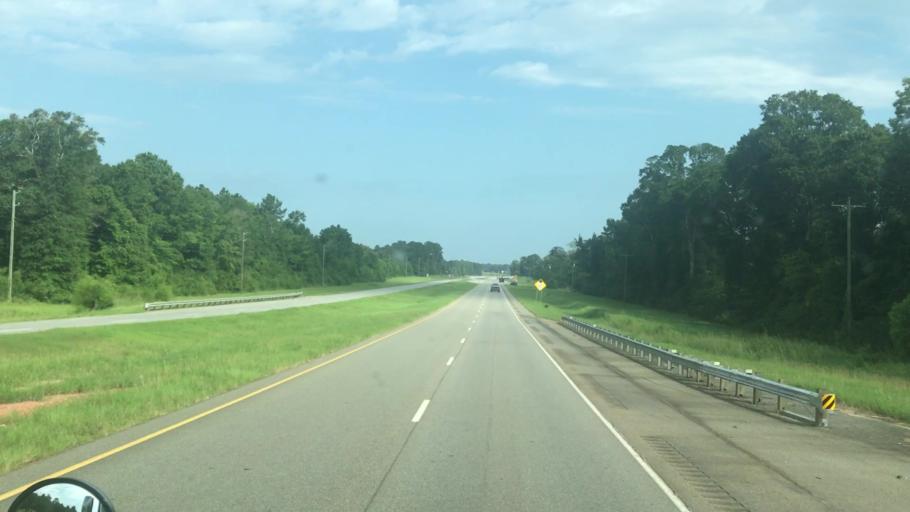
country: US
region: Georgia
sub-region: Early County
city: Blakely
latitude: 31.3468
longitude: -84.9123
